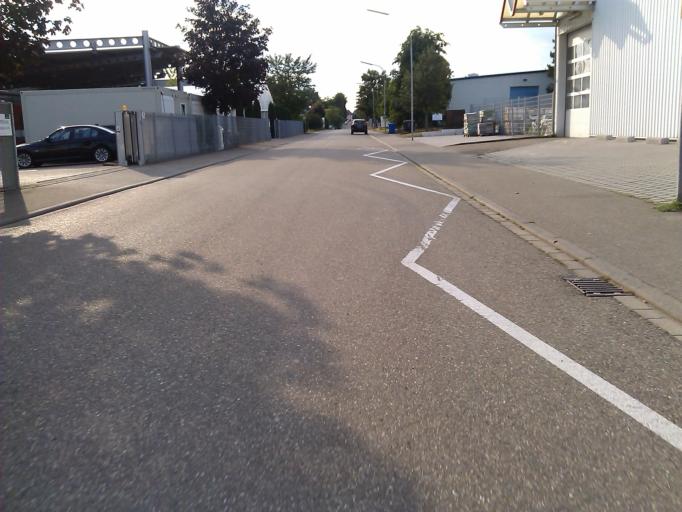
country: DE
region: Baden-Wuerttemberg
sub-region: Regierungsbezirk Stuttgart
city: Untereisesheim
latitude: 49.2287
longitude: 9.2013
